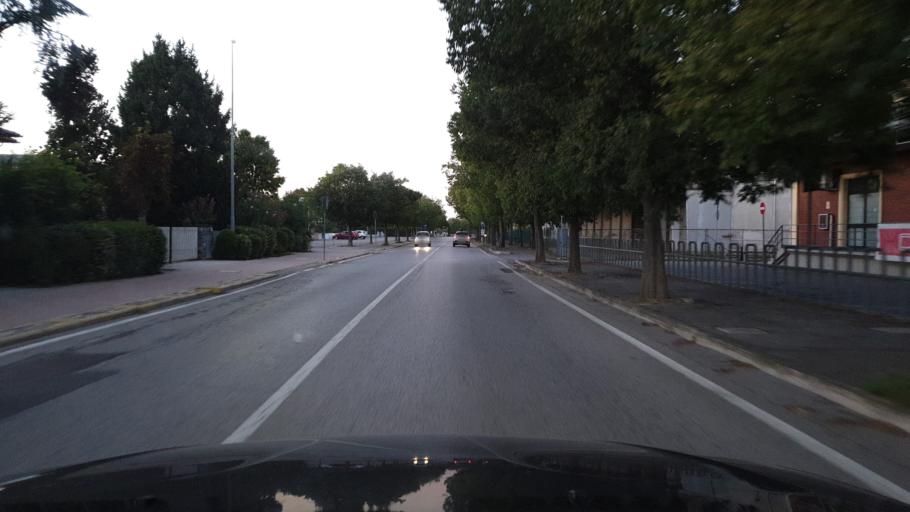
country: IT
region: Emilia-Romagna
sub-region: Provincia di Bologna
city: Altedo
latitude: 44.6715
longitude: 11.4902
